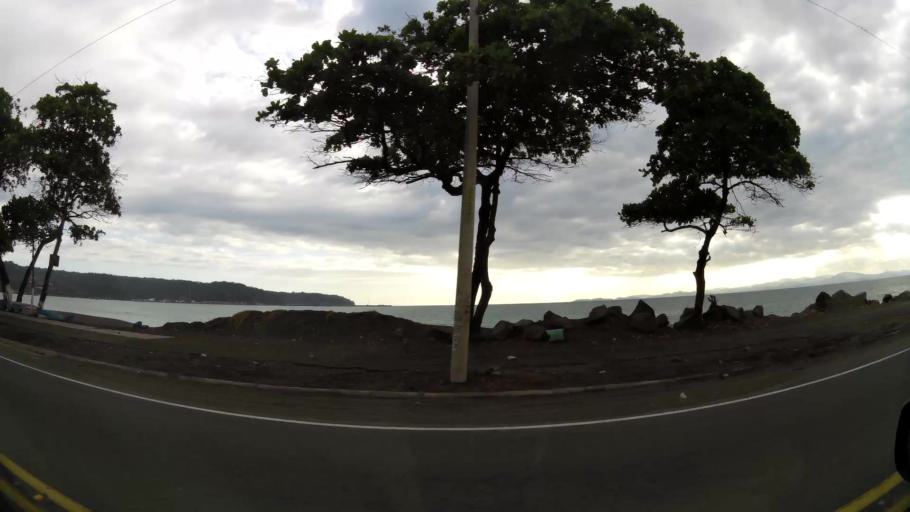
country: CR
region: Puntarenas
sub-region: Canton Central de Puntarenas
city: Chacarita
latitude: 9.9324
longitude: -84.7209
